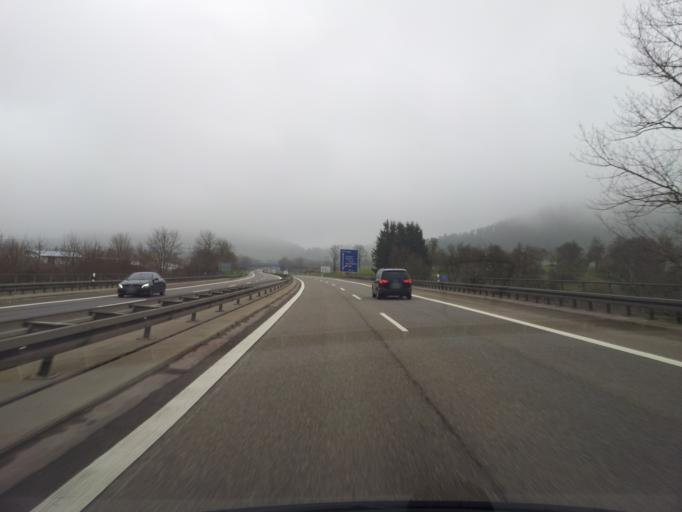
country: DE
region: Baden-Wuerttemberg
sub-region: Freiburg Region
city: Hilzingen
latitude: 47.7565
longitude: 8.7877
